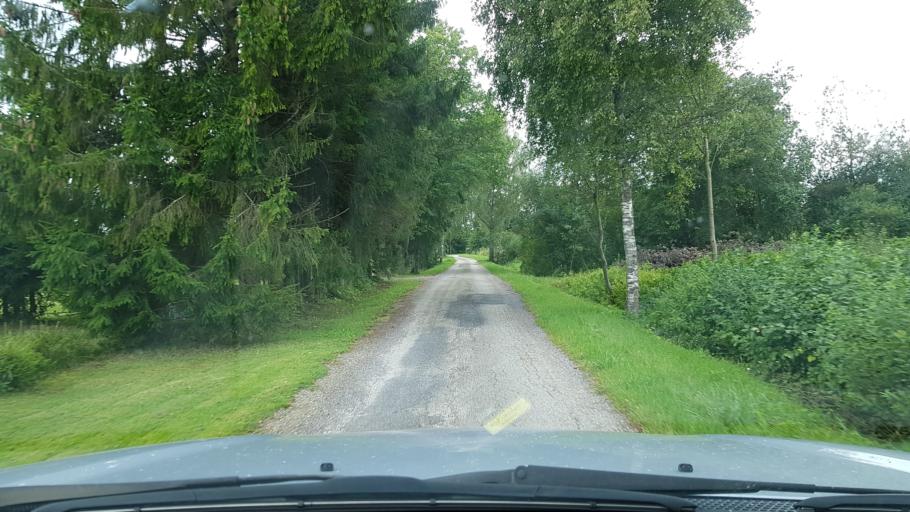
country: EE
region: Harju
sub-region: Raasiku vald
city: Arukula
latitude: 59.2906
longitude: 25.0751
